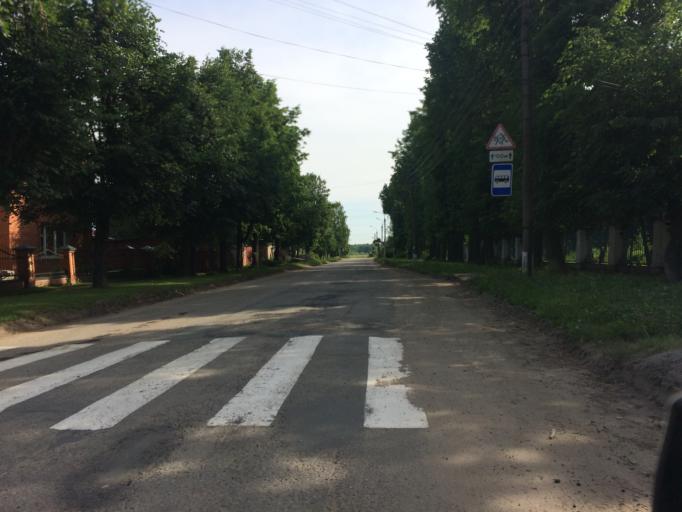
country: RU
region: Mariy-El
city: Yoshkar-Ola
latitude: 56.6506
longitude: 47.9135
